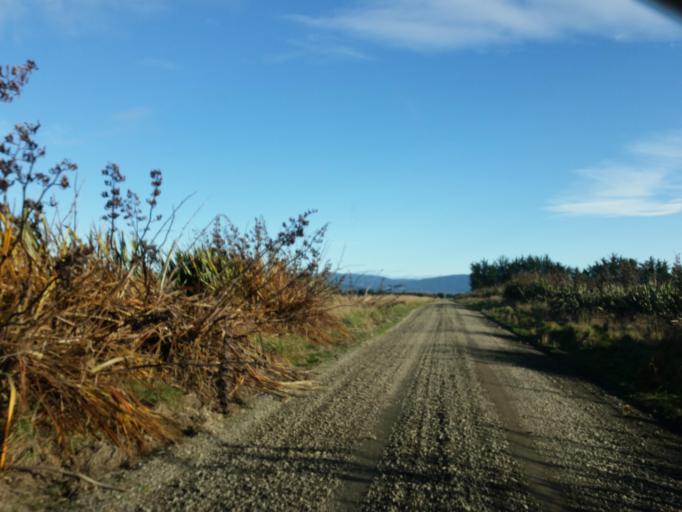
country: NZ
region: Southland
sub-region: Southland District
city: Winton
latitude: -46.1393
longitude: 168.1117
